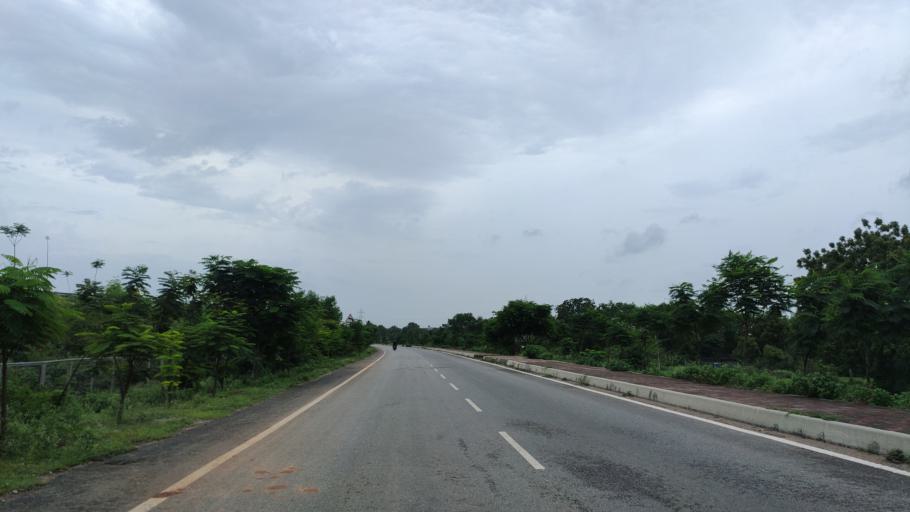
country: IN
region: Telangana
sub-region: Rangareddi
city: Secunderabad
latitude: 17.5786
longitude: 78.5959
